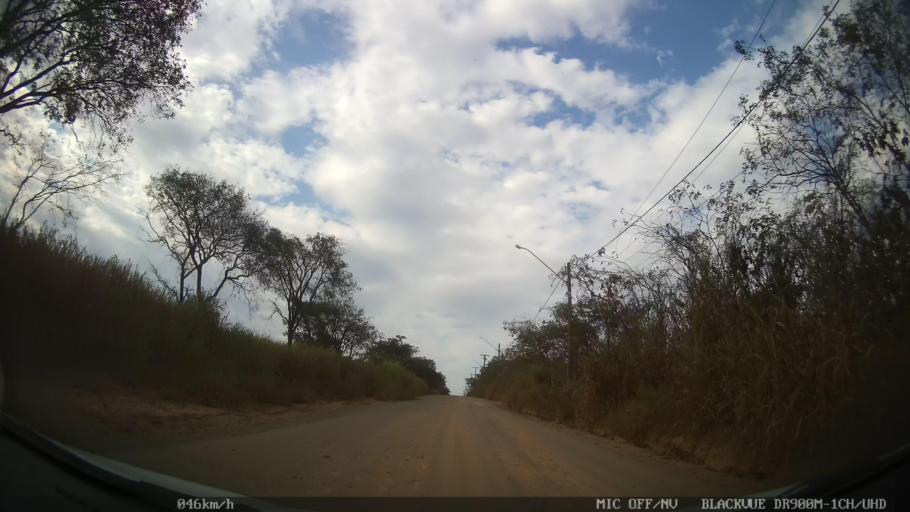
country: BR
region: Sao Paulo
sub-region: Paulinia
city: Paulinia
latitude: -22.7164
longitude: -47.1536
